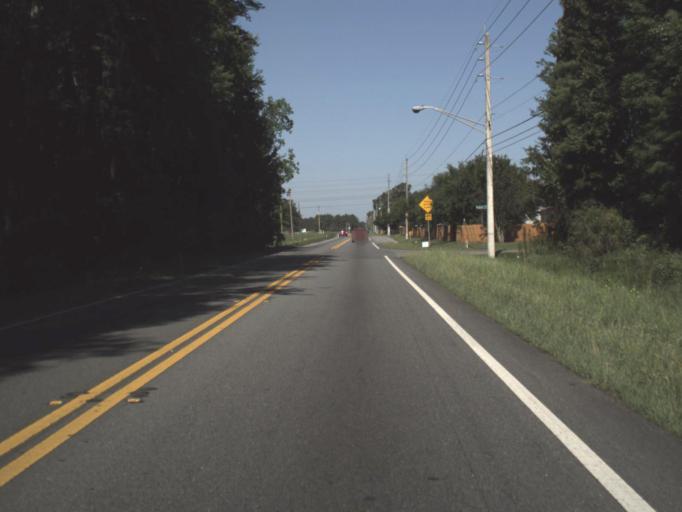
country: US
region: Florida
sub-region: Clay County
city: Bellair-Meadowbrook Terrace
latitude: 30.3181
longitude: -81.8142
